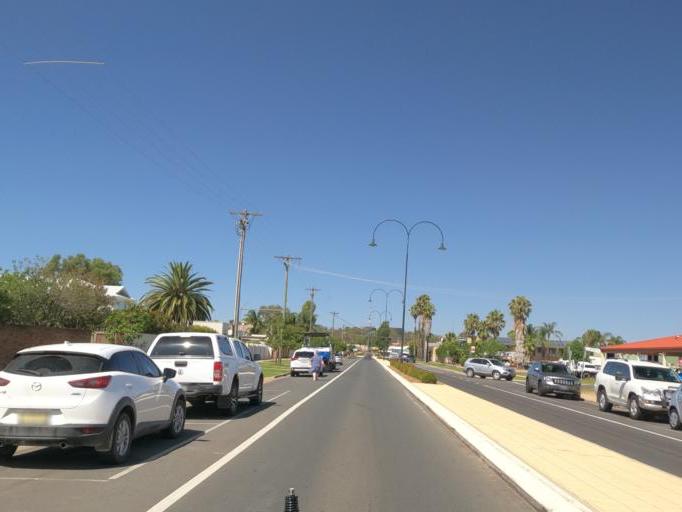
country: AU
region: New South Wales
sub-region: Corowa Shire
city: Mulwala
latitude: -35.9908
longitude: 146.0040
